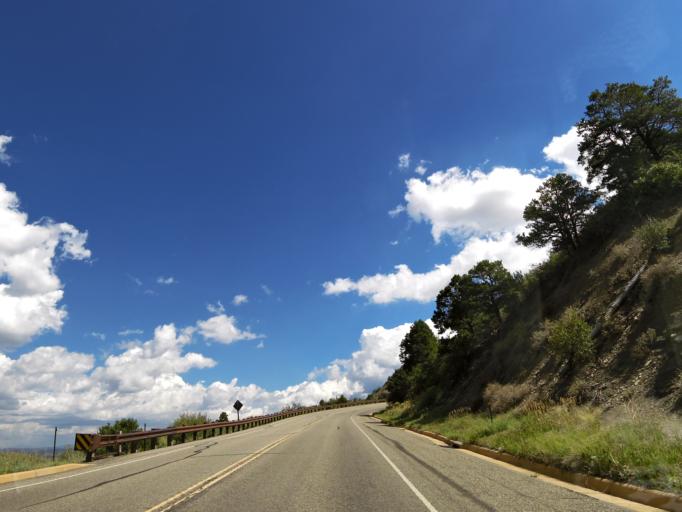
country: US
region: Colorado
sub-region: Montezuma County
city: Mancos
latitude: 37.3219
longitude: -108.4174
